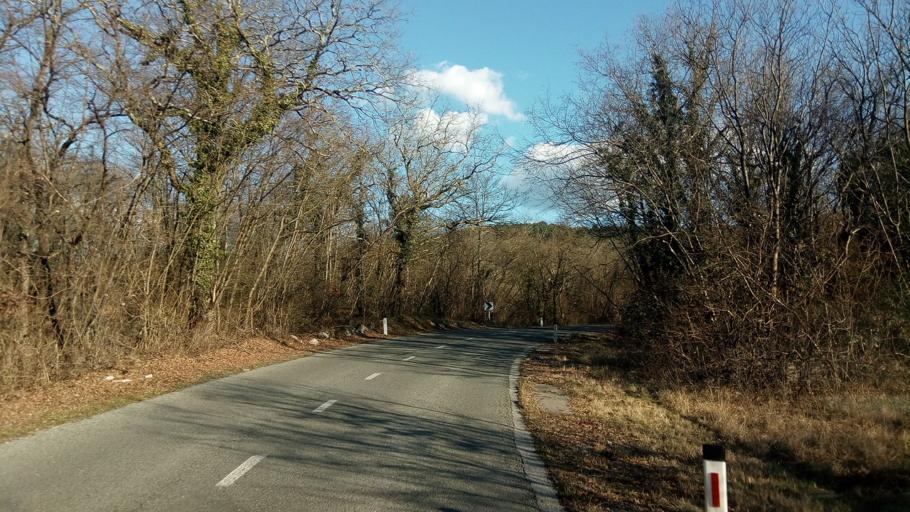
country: SI
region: Sezana
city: Sezana
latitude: 45.7945
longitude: 13.8580
